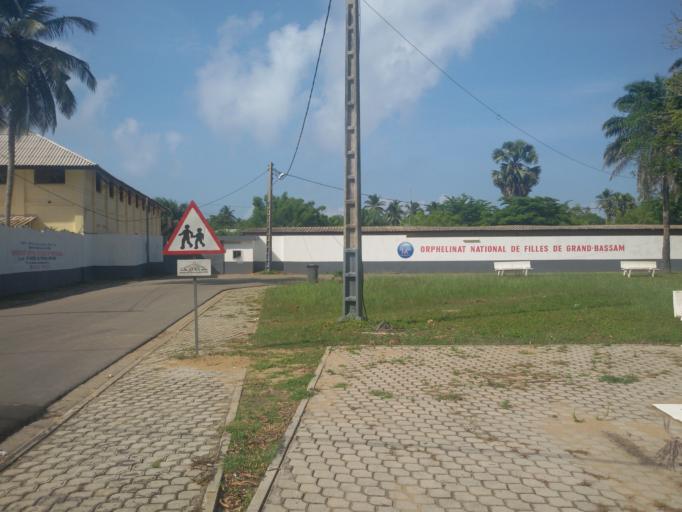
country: CI
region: Sud-Comoe
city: Grand-Bassam
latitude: 5.1975
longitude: -3.7358
